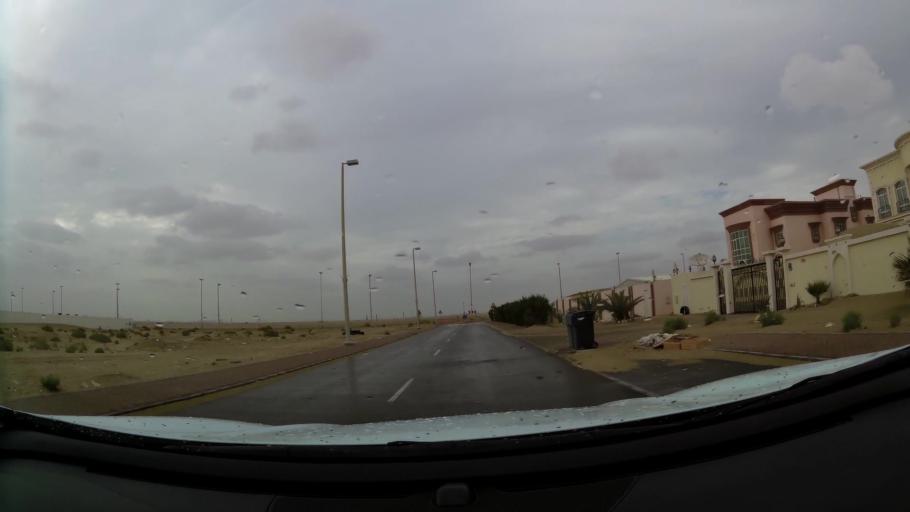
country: AE
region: Abu Dhabi
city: Abu Dhabi
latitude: 24.3665
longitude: 54.6226
